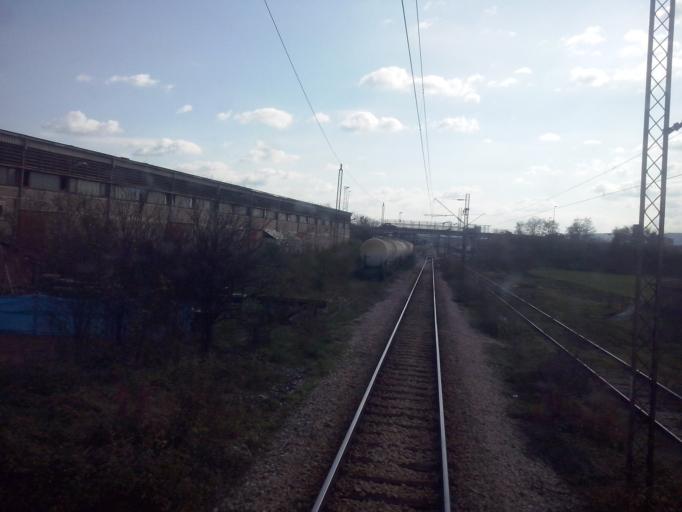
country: RS
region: Central Serbia
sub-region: Zlatiborski Okrug
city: Pozega
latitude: 43.8476
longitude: 20.0206
